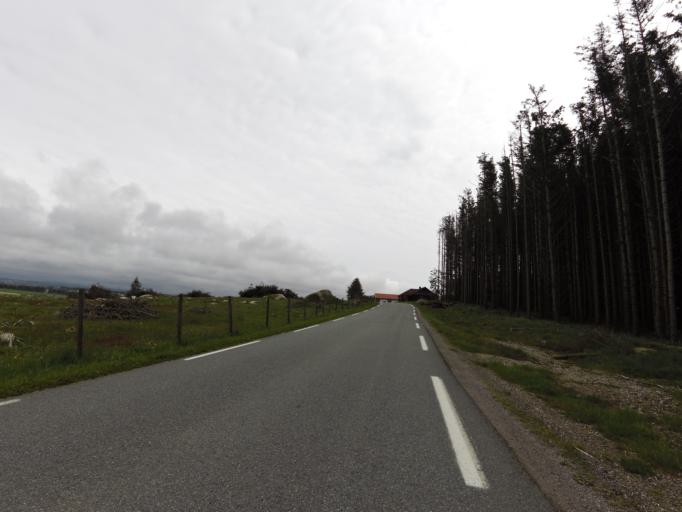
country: NO
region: Rogaland
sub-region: Ha
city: Naerbo
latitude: 58.6607
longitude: 5.5592
